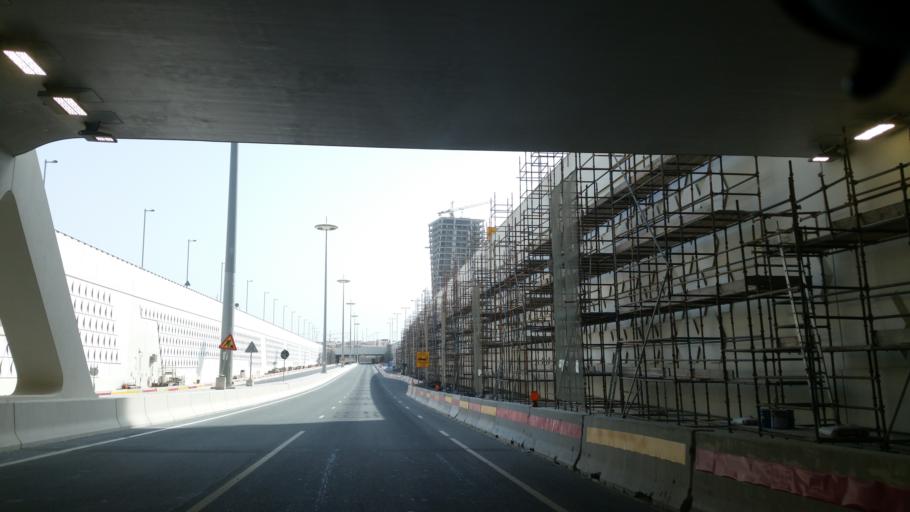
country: QA
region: Baladiyat Umm Salal
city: Umm Salal Muhammad
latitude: 25.4300
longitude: 51.5118
